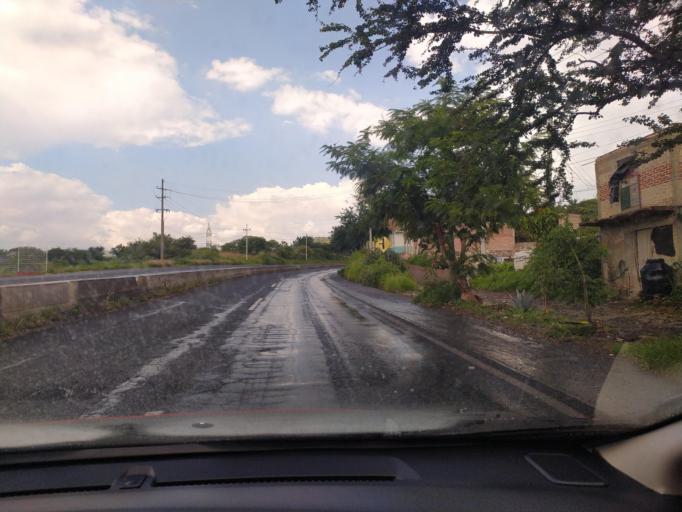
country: MX
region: Jalisco
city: Bellavista
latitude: 20.4324
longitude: -103.5997
